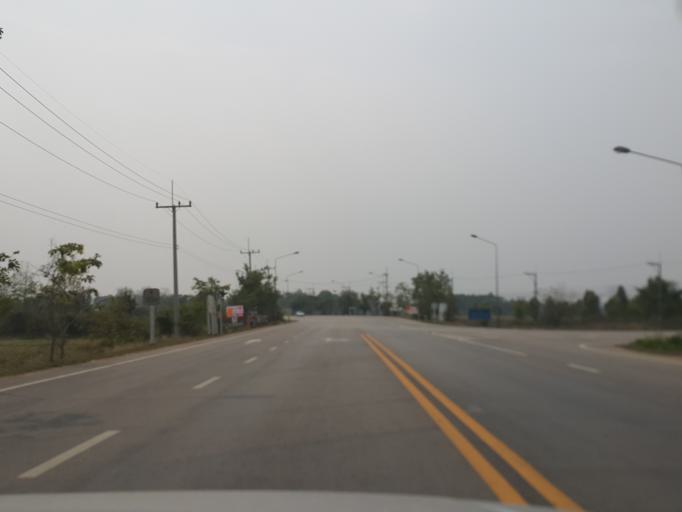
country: TH
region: Lampang
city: Ko Kha
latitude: 18.2085
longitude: 99.3906
